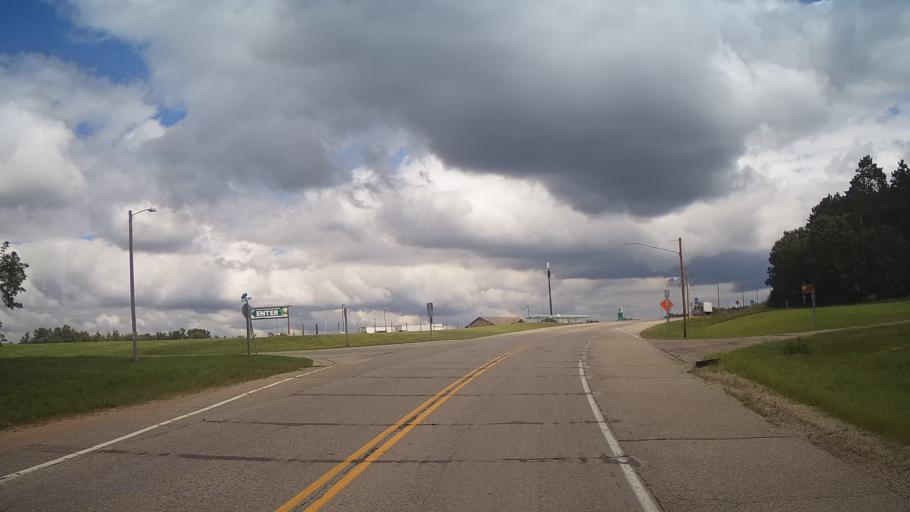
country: US
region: Wisconsin
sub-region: Marquette County
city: Westfield
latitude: 44.0338
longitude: -89.5371
